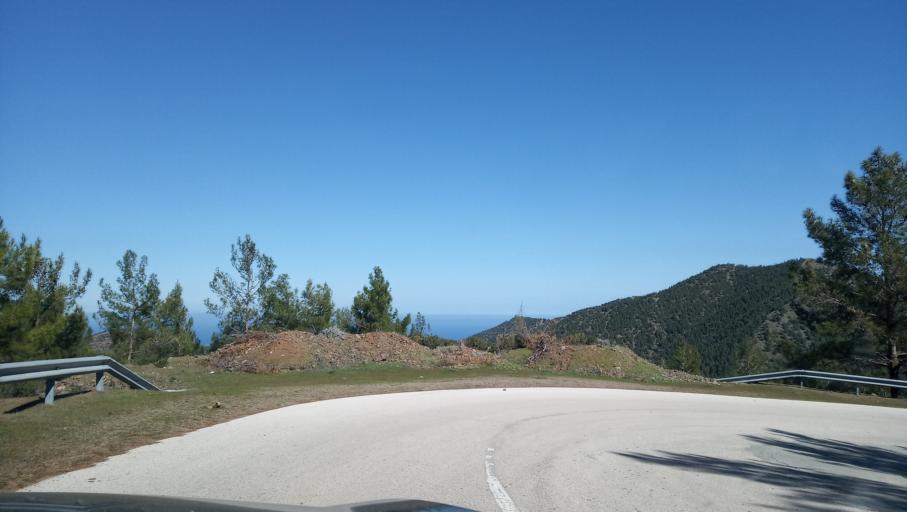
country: CY
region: Lefkosia
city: Lefka
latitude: 35.0715
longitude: 32.7597
